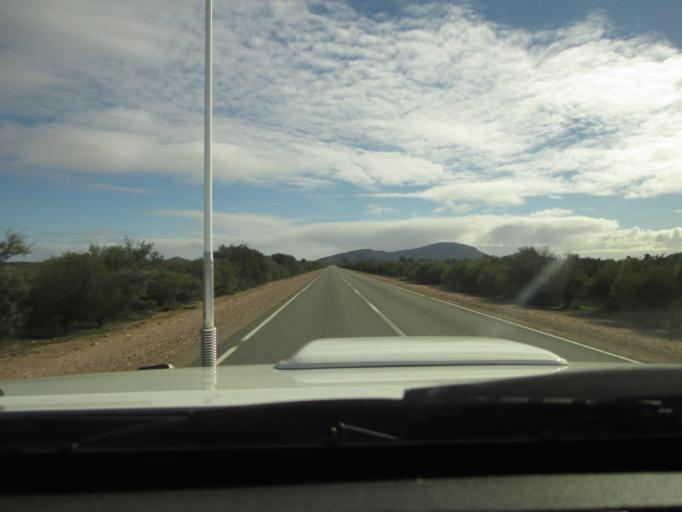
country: AU
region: South Australia
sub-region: Flinders Ranges
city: Quorn
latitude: -31.8403
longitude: 138.3907
